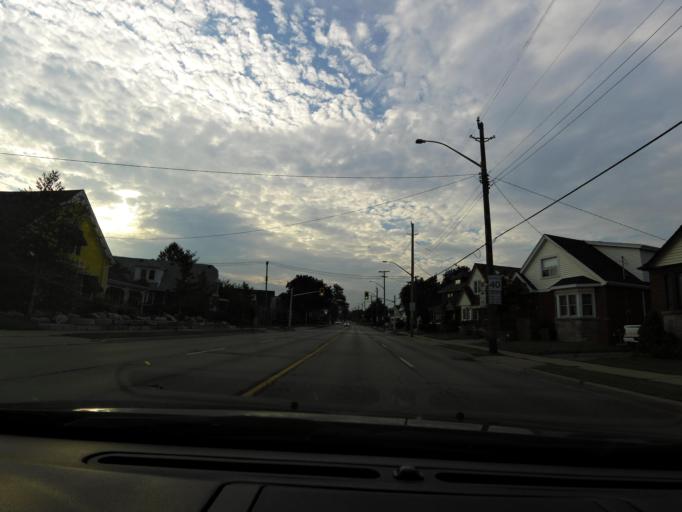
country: CA
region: Ontario
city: Hamilton
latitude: 43.2344
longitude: -79.8165
